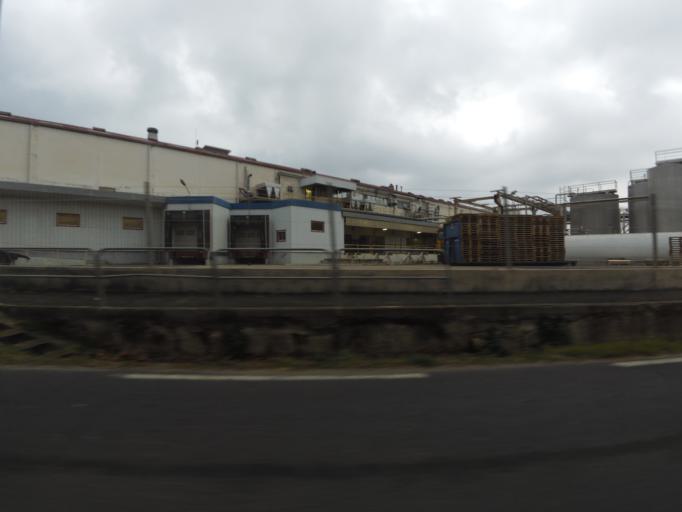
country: FR
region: Languedoc-Roussillon
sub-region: Departement du Gard
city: Aigues-Vives
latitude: 43.7271
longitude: 4.1920
